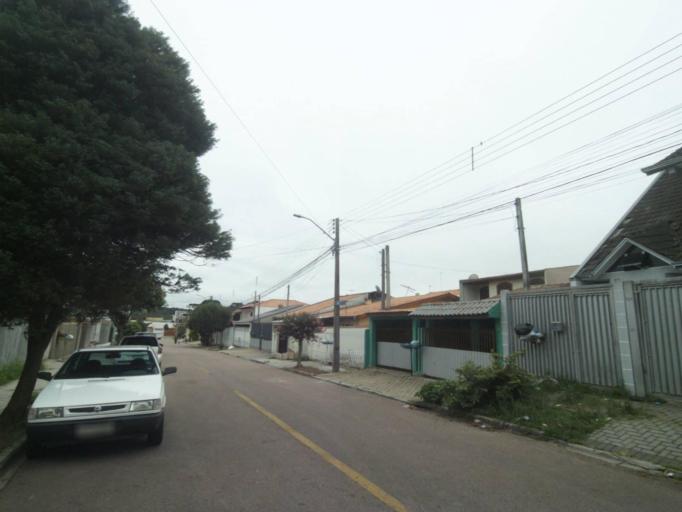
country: BR
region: Parana
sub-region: Araucaria
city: Araucaria
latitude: -25.5426
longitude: -49.3382
